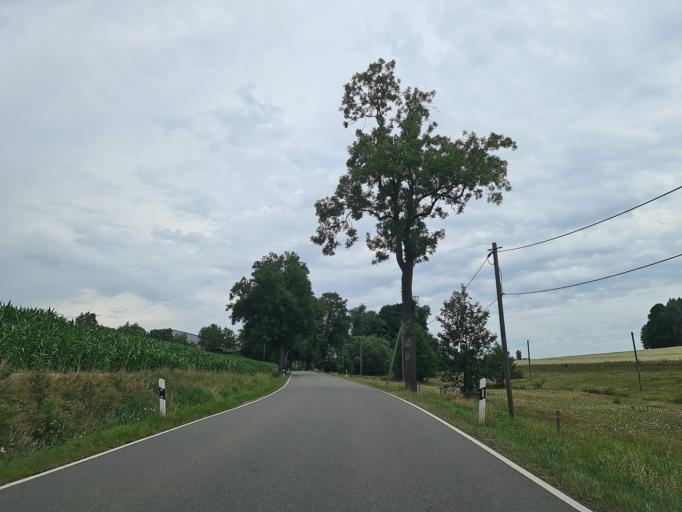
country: DE
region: Saxony
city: Pfaffroda
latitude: 50.7081
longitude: 13.3515
